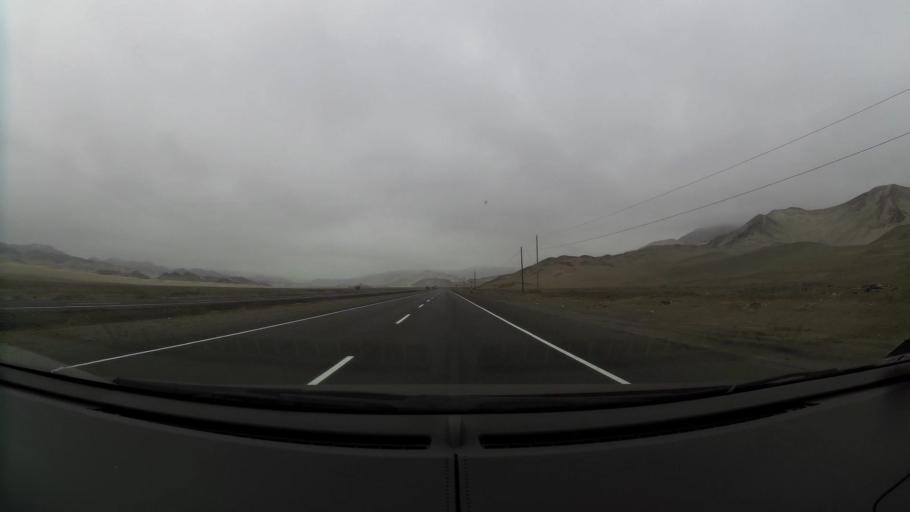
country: PE
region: La Libertad
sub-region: Viru
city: Guadalupito
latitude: -8.7628
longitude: -78.6343
